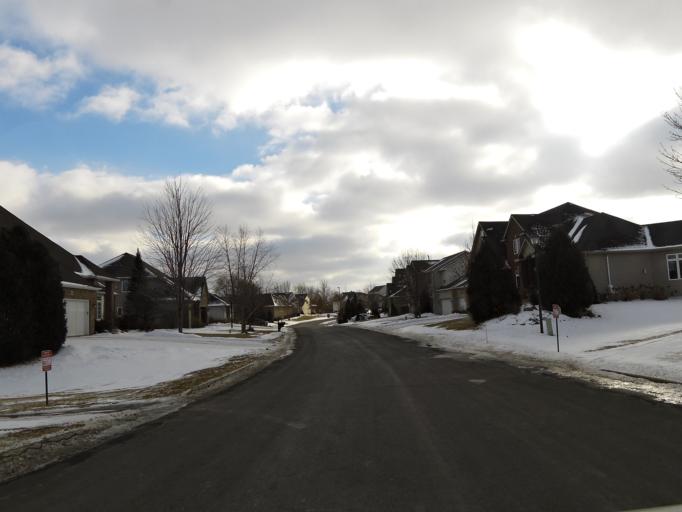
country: US
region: Minnesota
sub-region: Scott County
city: Prior Lake
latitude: 44.7299
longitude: -93.4548
